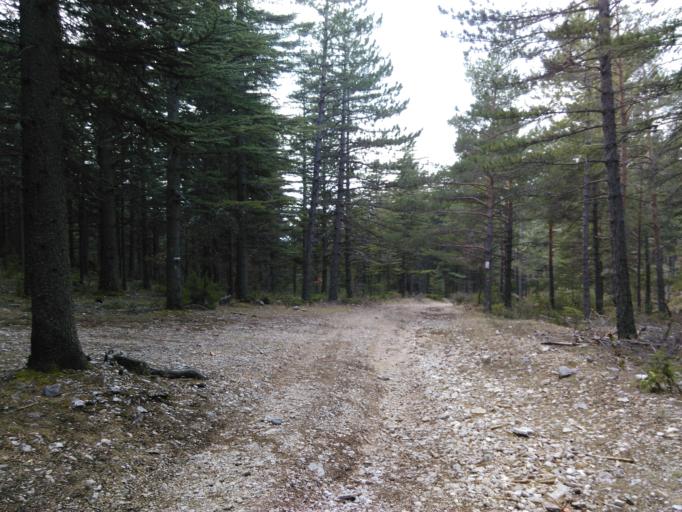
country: FR
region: Provence-Alpes-Cote d'Azur
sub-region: Departement du Vaucluse
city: Villes-sur-Auzon
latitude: 44.1354
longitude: 5.2735
